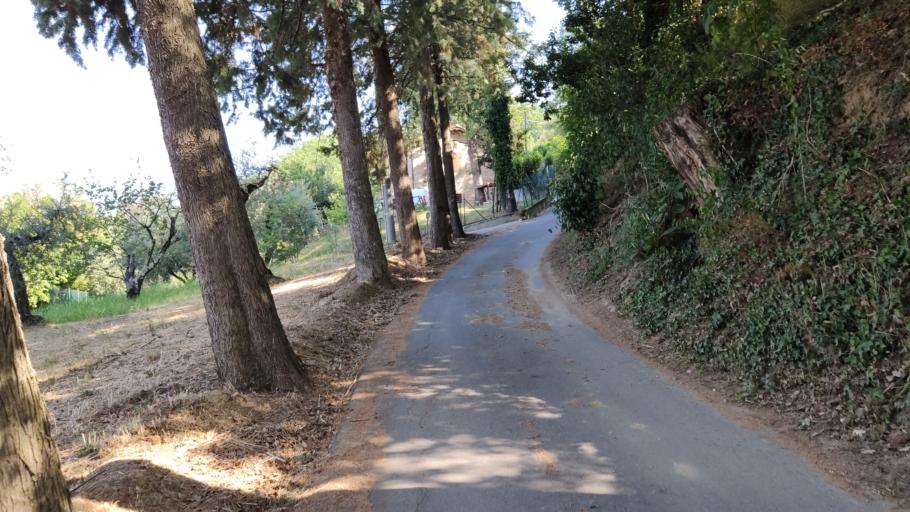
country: IT
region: Umbria
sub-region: Provincia di Terni
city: Amelia
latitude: 42.5320
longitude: 12.4101
